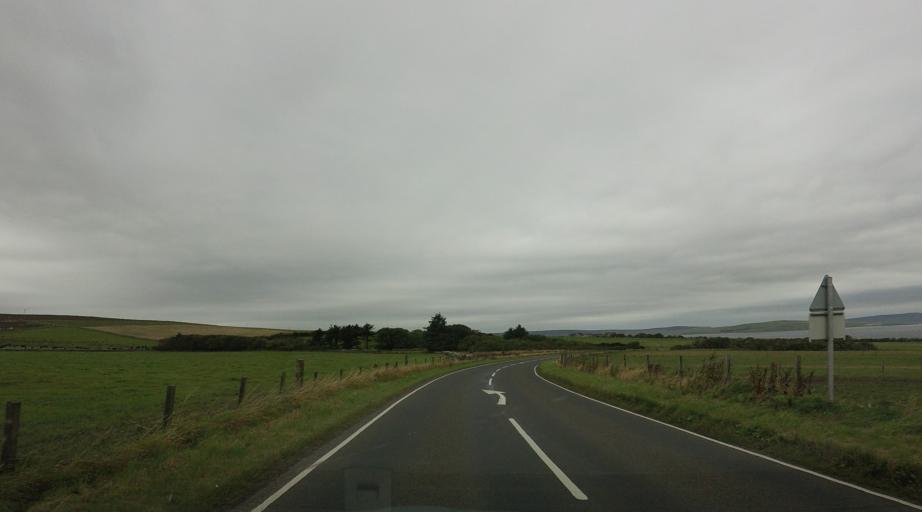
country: GB
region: Scotland
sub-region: Orkney Islands
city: Orkney
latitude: 58.9921
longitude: -2.9924
